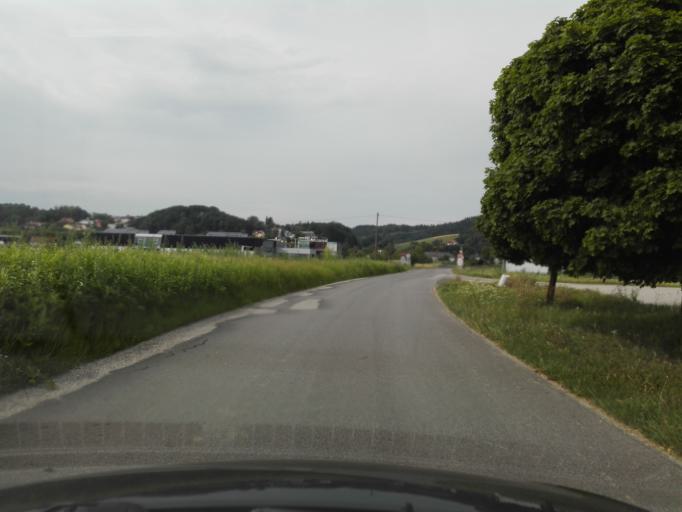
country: AT
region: Upper Austria
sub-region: Politischer Bezirk Perg
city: Bad Kreuzen
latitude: 48.2071
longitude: 14.7591
